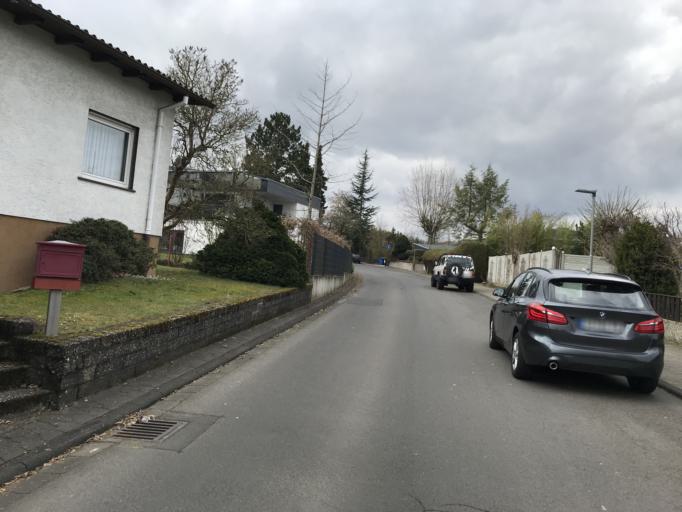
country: DE
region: Hesse
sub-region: Regierungsbezirk Giessen
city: Lich
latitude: 50.5270
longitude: 8.8112
